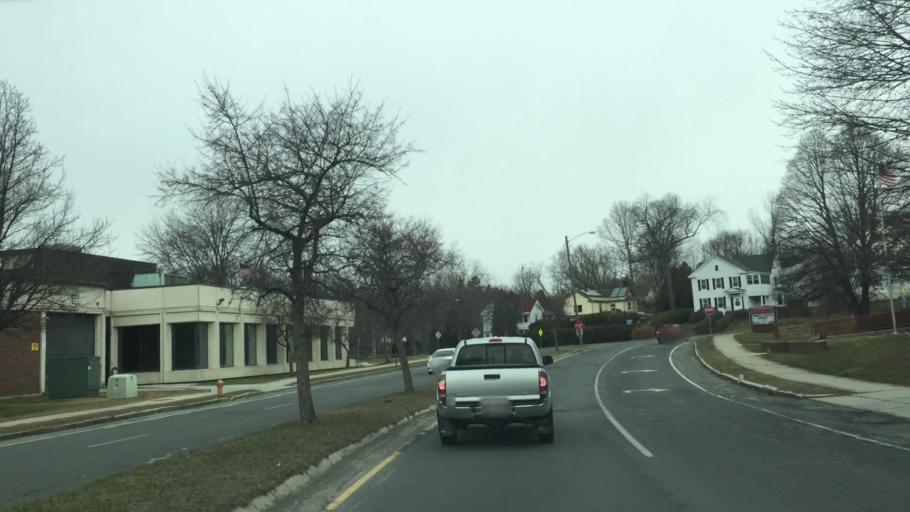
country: US
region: Massachusetts
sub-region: Berkshire County
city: Pittsfield
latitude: 42.4488
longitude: -73.2617
